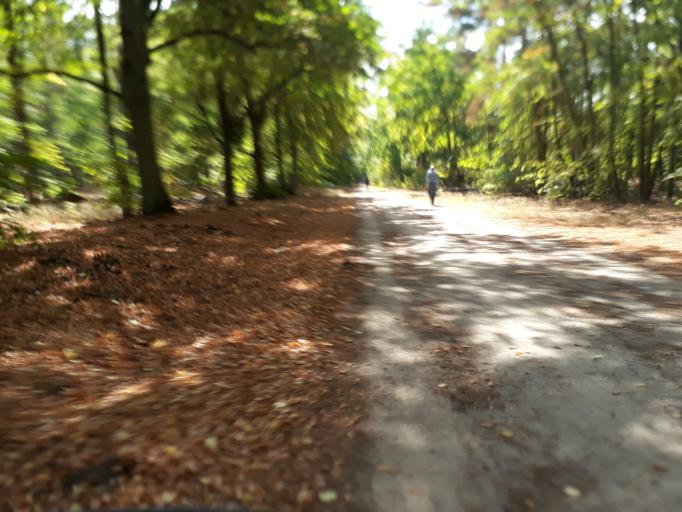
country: DE
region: Berlin
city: Grunewald
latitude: 52.4855
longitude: 13.2423
